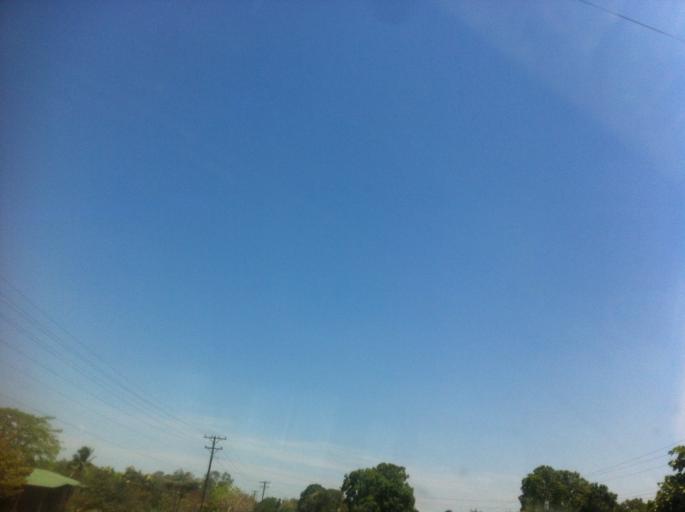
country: CR
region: Guanacaste
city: Belen
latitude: 10.4475
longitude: -85.5552
